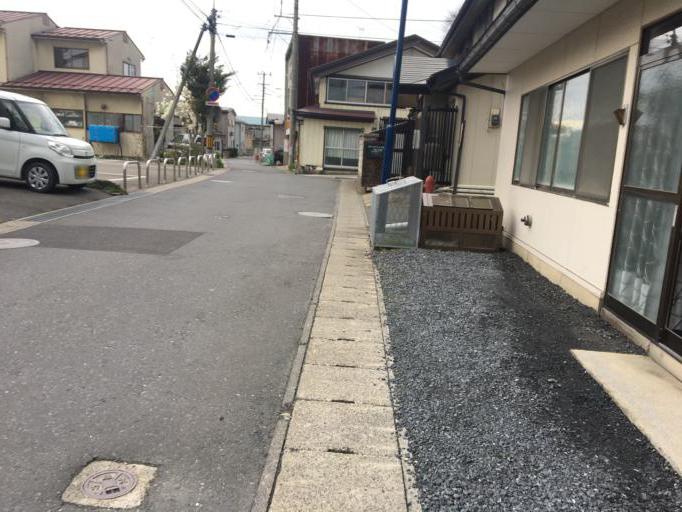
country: JP
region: Aomori
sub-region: Hachinohe Shi
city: Uchimaru
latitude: 40.5247
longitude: 141.5229
